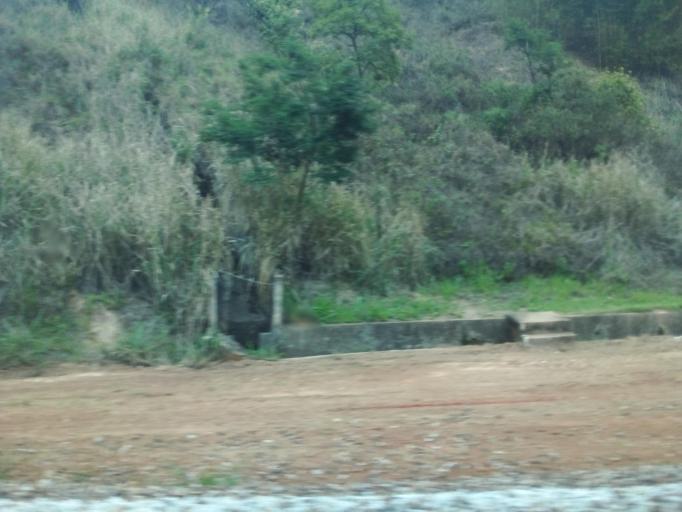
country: BR
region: Minas Gerais
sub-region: Rio Piracicaba
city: Rio Piracicaba
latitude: -19.8740
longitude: -43.1203
